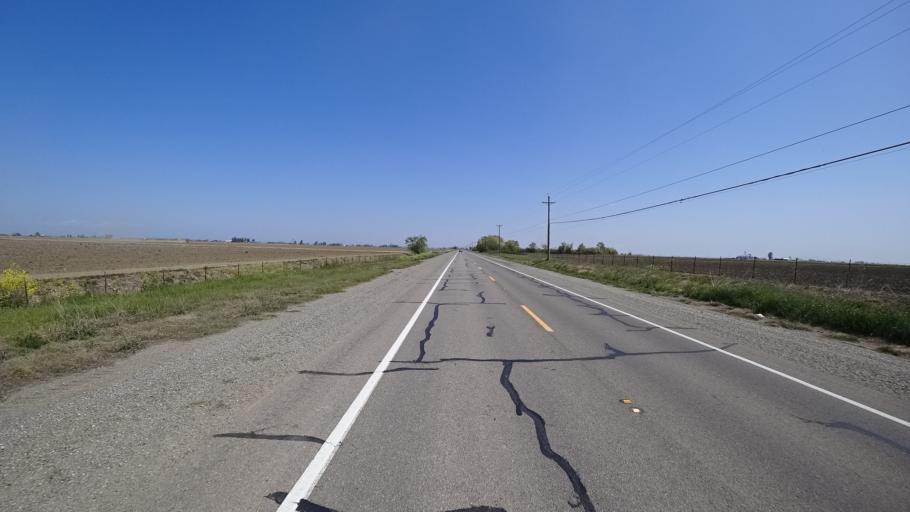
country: US
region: California
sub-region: Glenn County
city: Willows
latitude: 39.5242
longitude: -122.1572
